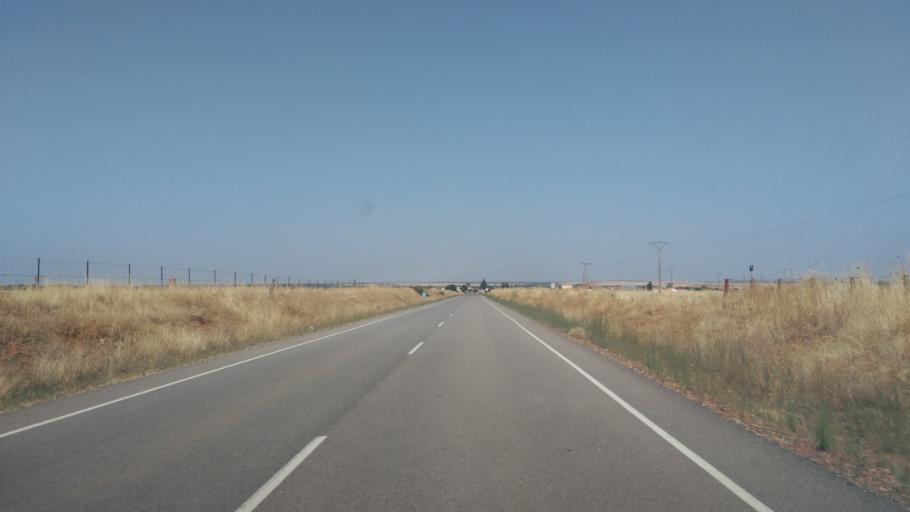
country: ES
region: Castille and Leon
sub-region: Provincia de Salamanca
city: Abusejo
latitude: 40.7015
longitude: -6.1369
